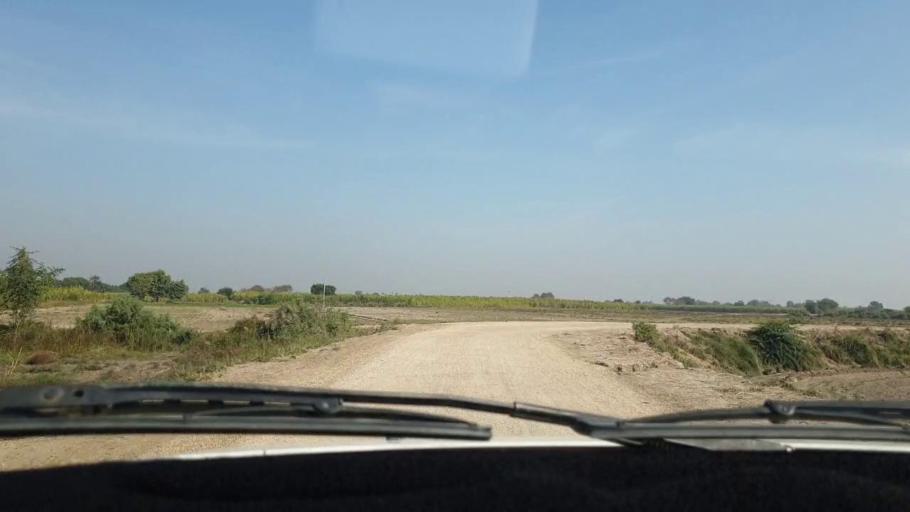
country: PK
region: Sindh
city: Tando Muhammad Khan
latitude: 24.9903
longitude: 68.4682
